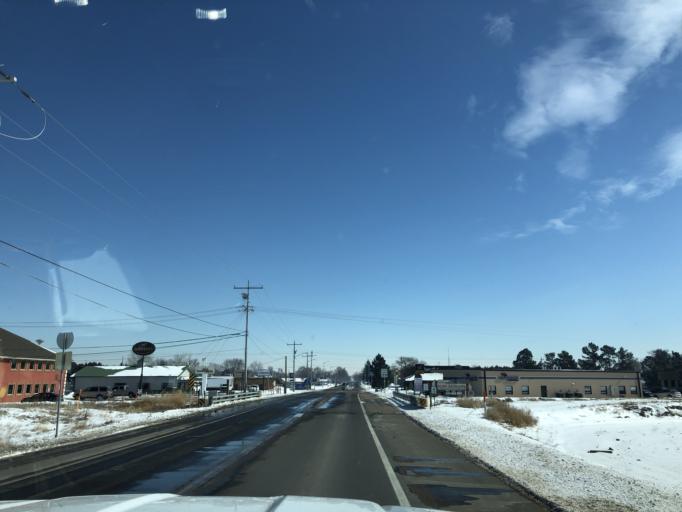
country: US
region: Colorado
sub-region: Morgan County
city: Fort Morgan
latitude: 40.2540
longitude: -103.8178
